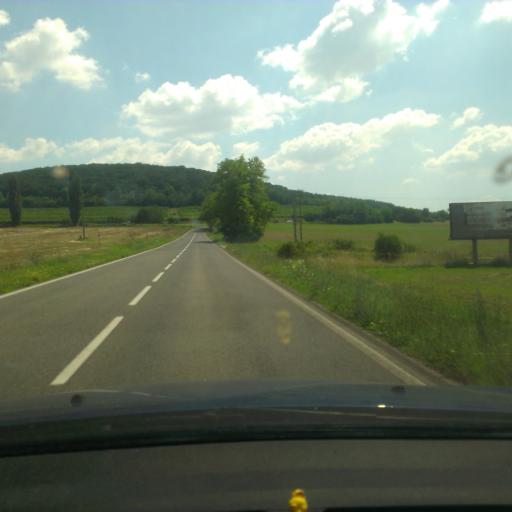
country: SK
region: Trnavsky
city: Hlohovec
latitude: 48.4636
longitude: 17.8147
